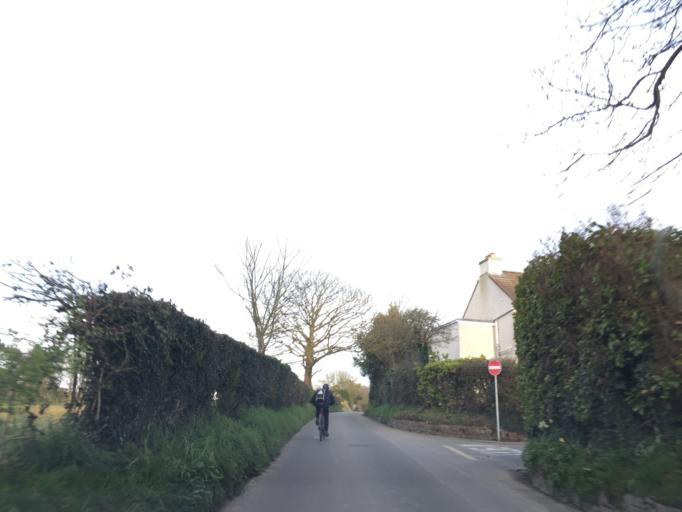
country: JE
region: St Helier
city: Saint Helier
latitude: 49.2284
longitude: -2.0685
